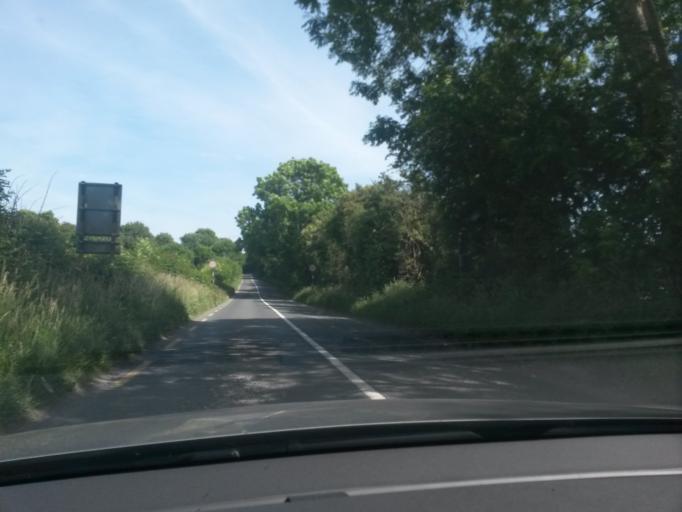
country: IE
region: Leinster
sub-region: Kildare
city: Johnstown
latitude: 53.1996
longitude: -6.6173
